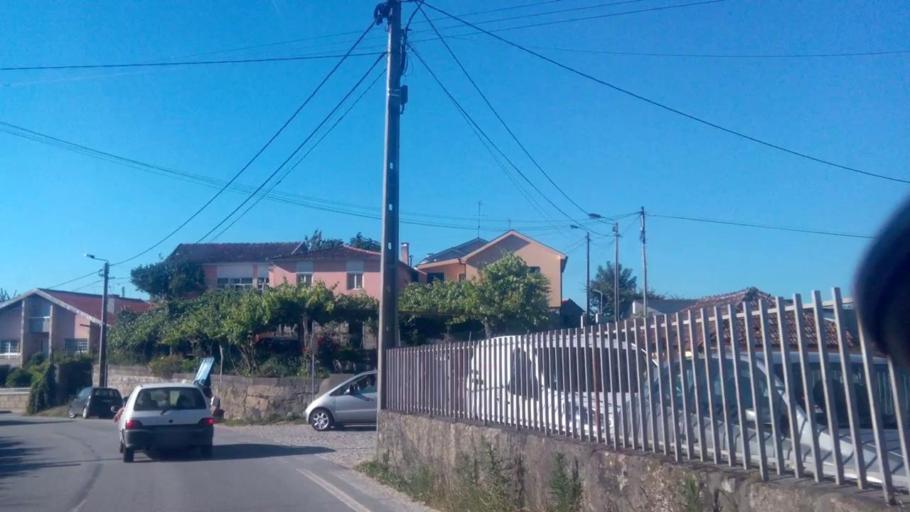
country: PT
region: Porto
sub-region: Penafiel
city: Penafiel
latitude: 41.1945
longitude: -8.2726
